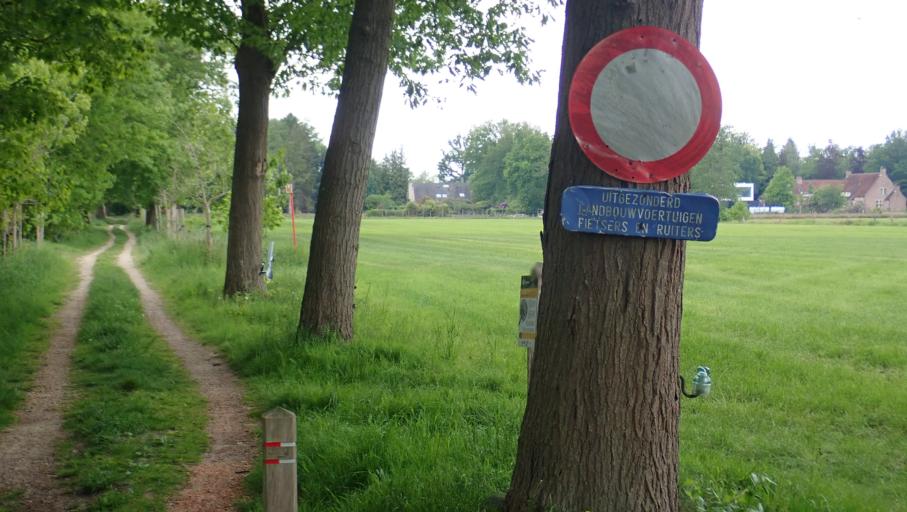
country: BE
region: Flanders
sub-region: Provincie Antwerpen
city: Zoersel
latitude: 51.2771
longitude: 4.6748
